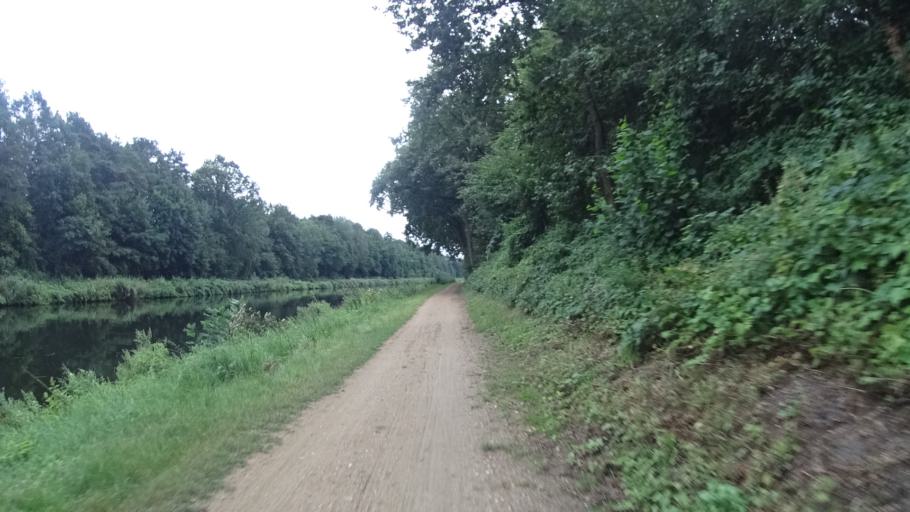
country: DE
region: Schleswig-Holstein
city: Molln
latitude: 53.6156
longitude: 10.6728
